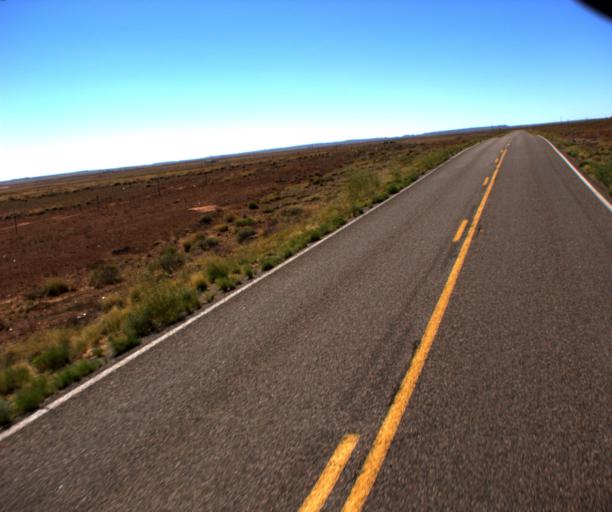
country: US
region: Arizona
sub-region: Coconino County
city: LeChee
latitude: 35.1857
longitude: -110.9334
